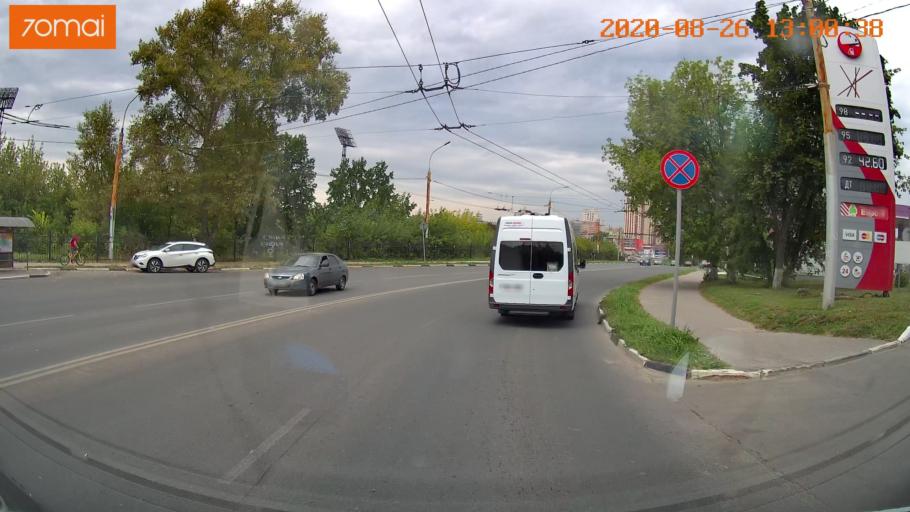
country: RU
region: Rjazan
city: Ryazan'
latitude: 54.6153
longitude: 39.7401
